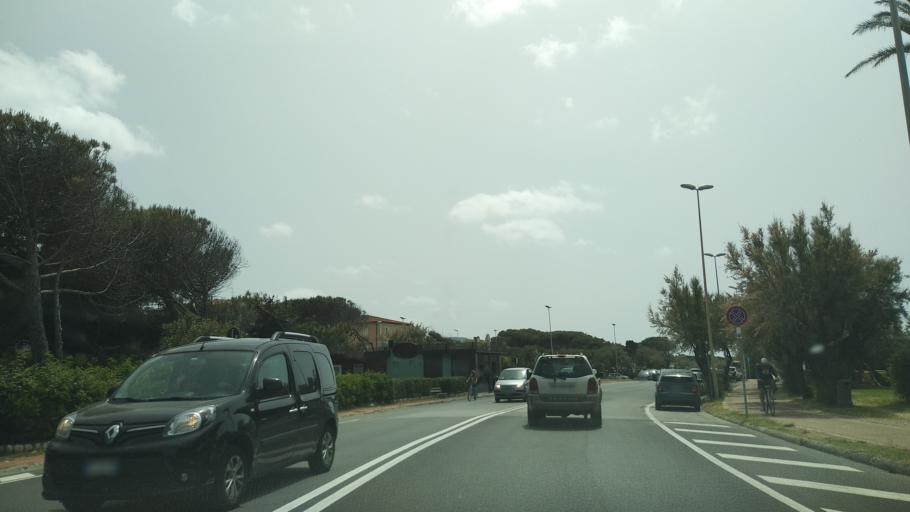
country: IT
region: Tuscany
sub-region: Provincia di Livorno
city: Livorno
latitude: 43.5186
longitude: 10.3162
